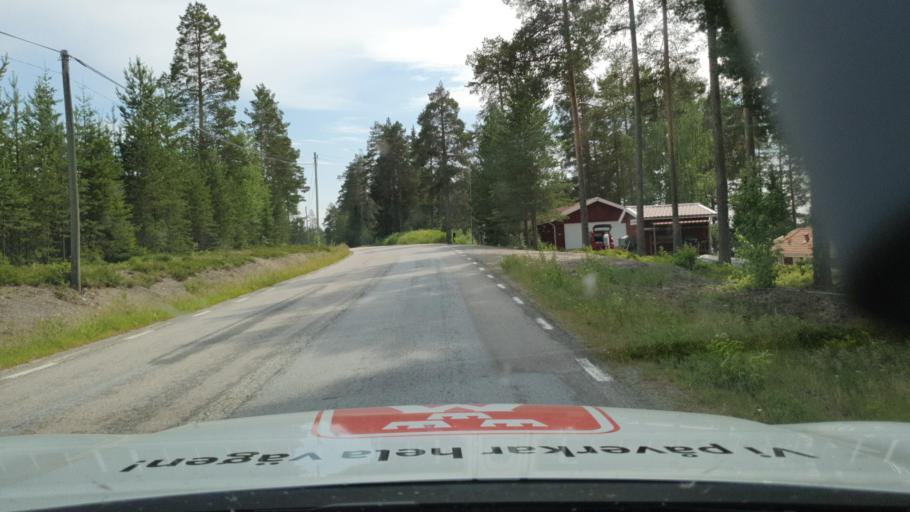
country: SE
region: Vaesterbotten
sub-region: Umea Kommun
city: Roback
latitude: 63.9043
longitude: 20.1532
